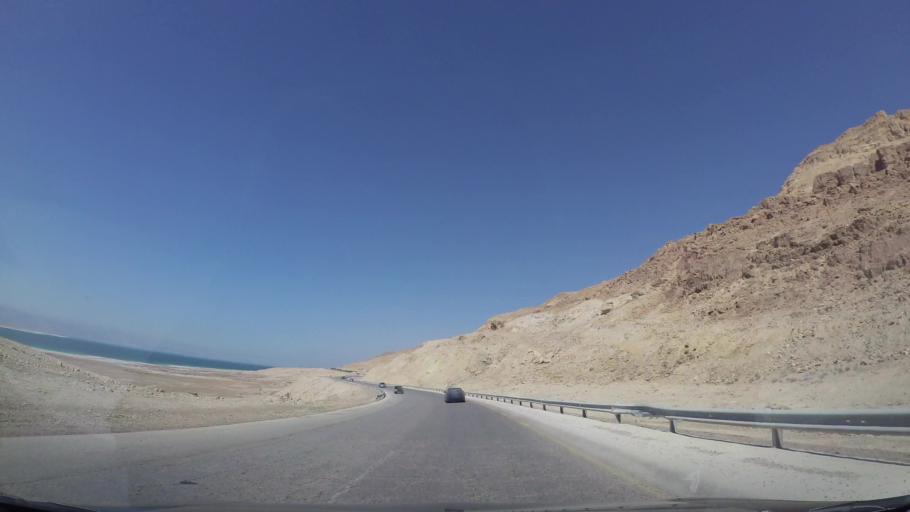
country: JO
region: Karak
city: Al Qasr
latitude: 31.3336
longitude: 35.5479
